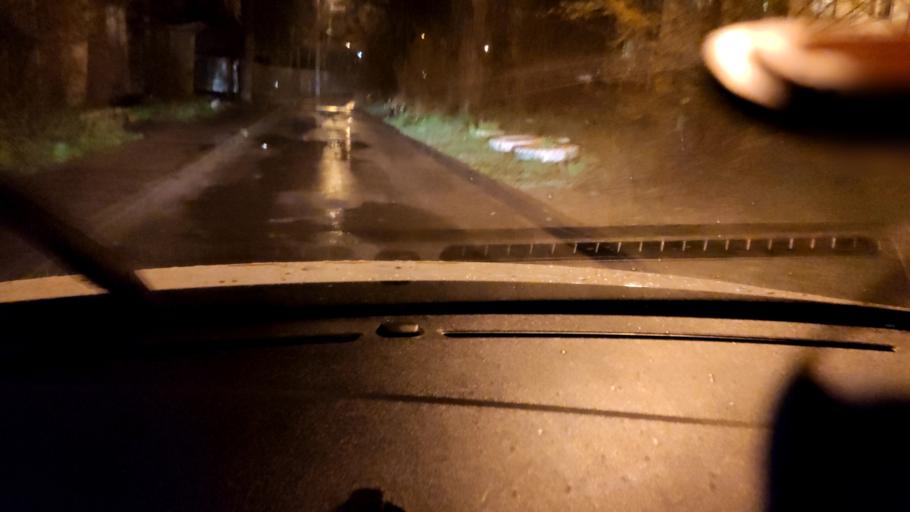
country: RU
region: Voronezj
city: Pridonskoy
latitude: 51.6243
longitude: 39.0717
